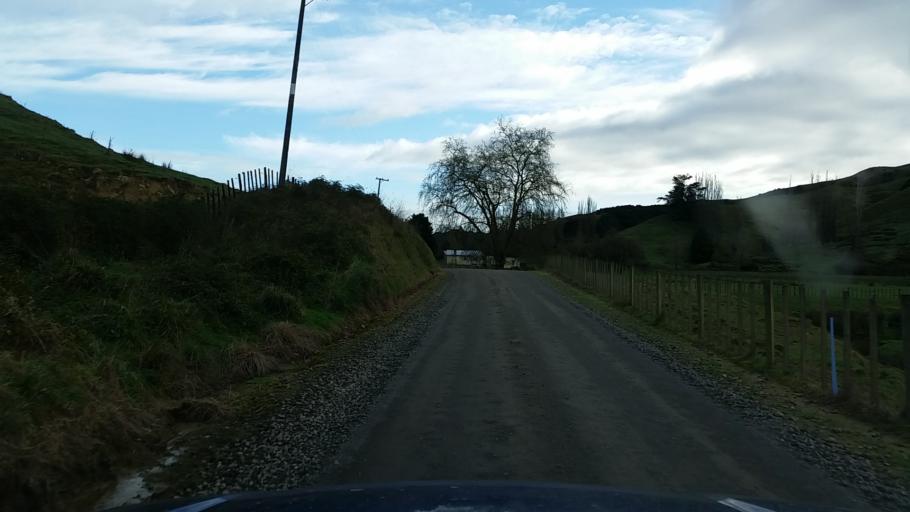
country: NZ
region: Taranaki
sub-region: New Plymouth District
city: Waitara
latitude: -39.0870
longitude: 174.8315
